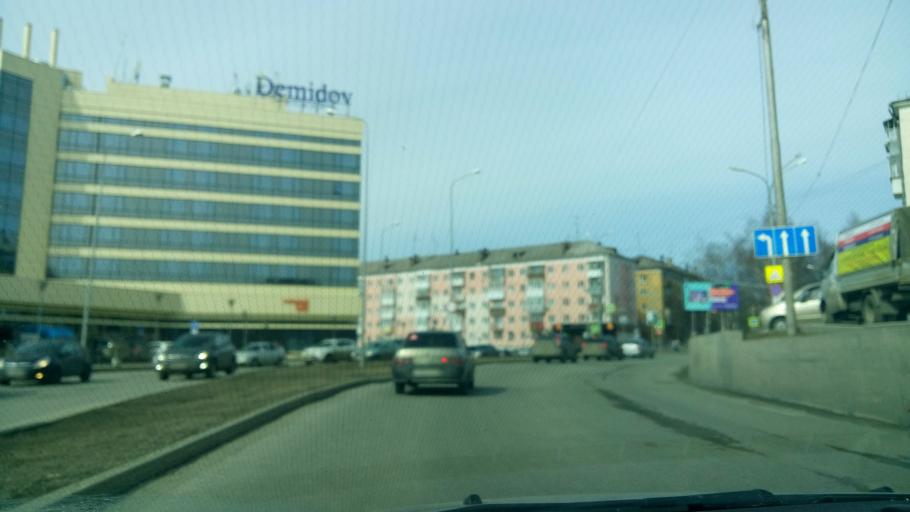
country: RU
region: Sverdlovsk
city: Nizhniy Tagil
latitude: 57.9053
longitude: 59.9854
